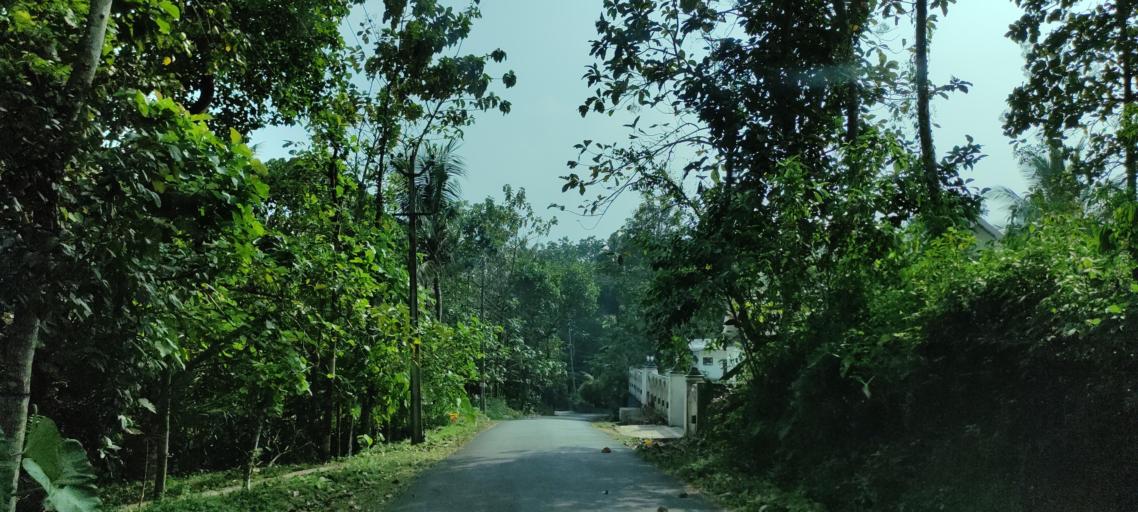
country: IN
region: Kerala
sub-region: Ernakulam
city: Piravam
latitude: 9.8046
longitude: 76.5255
